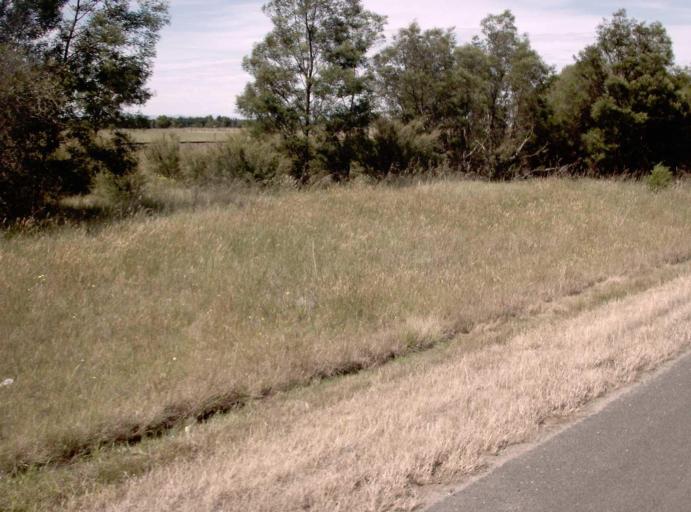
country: AU
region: Victoria
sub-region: Wellington
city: Sale
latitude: -38.1017
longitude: 146.9472
